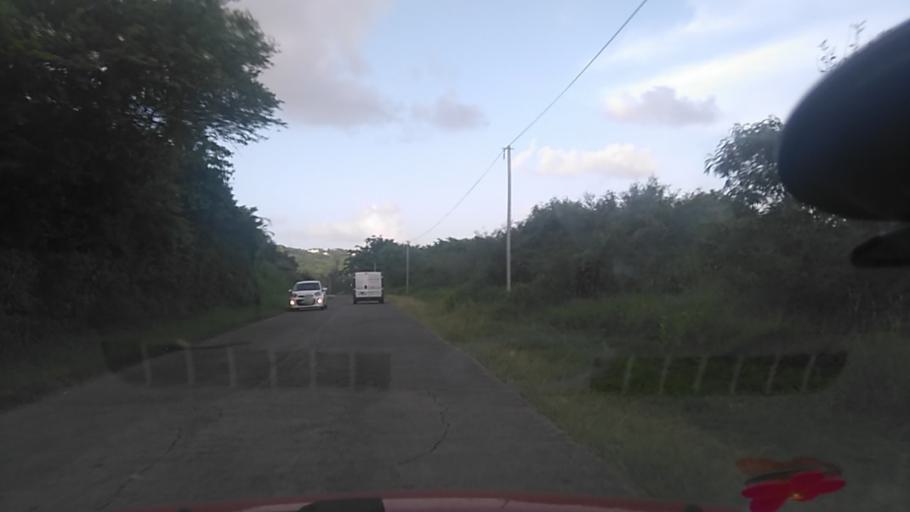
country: MQ
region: Martinique
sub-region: Martinique
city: Le Marin
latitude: 14.4674
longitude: -60.8618
